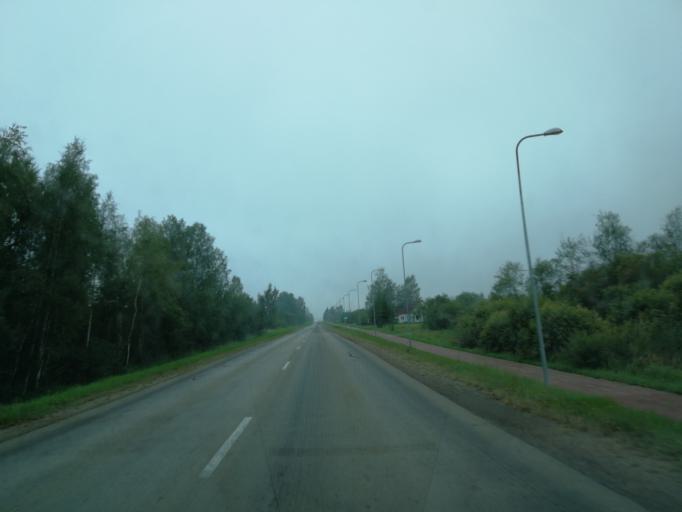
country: LV
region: Preilu Rajons
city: Preili
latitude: 56.2987
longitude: 26.6998
